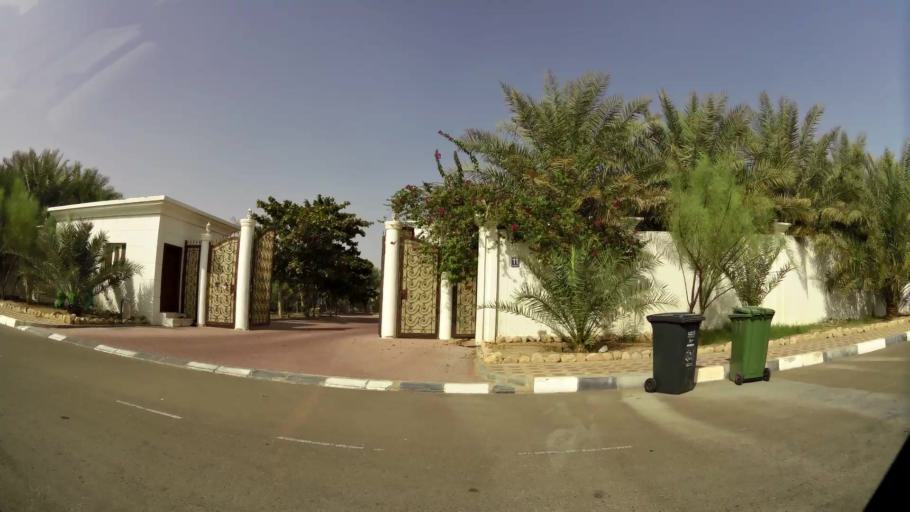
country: AE
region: Abu Dhabi
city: Al Ain
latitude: 24.2411
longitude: 55.6851
